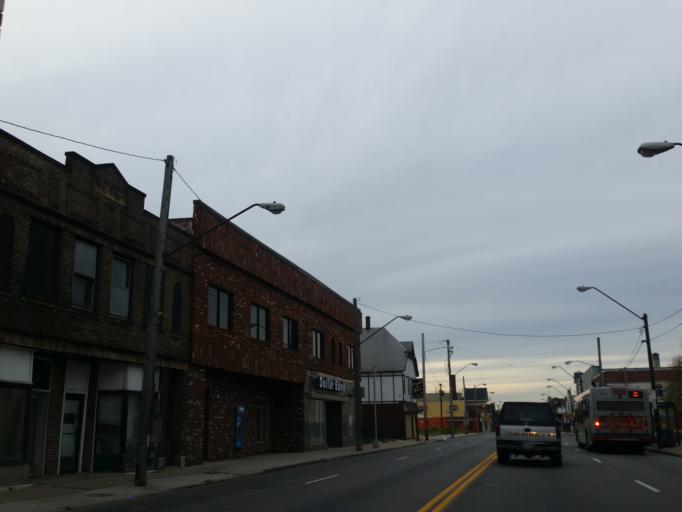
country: US
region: Ohio
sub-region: Cuyahoga County
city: Cleveland
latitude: 41.4697
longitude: -81.6998
